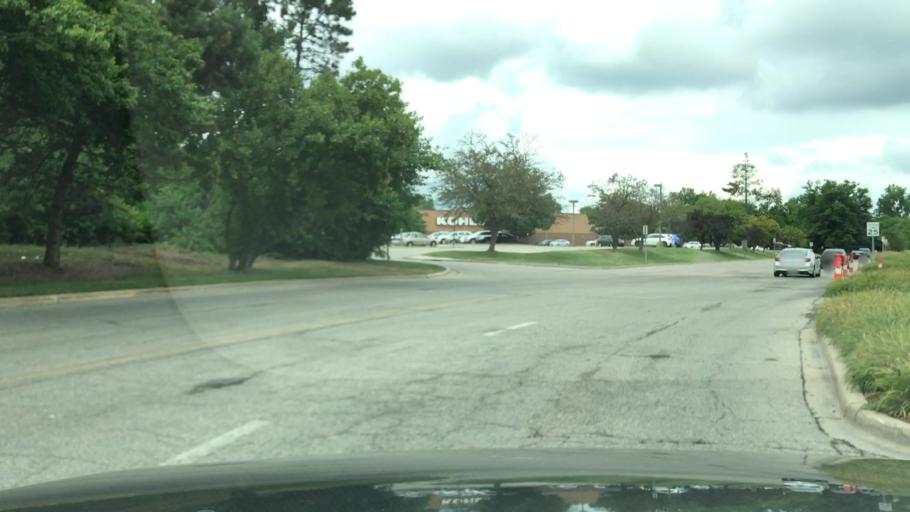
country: US
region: Michigan
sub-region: Kent County
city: East Grand Rapids
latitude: 42.9171
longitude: -85.5921
